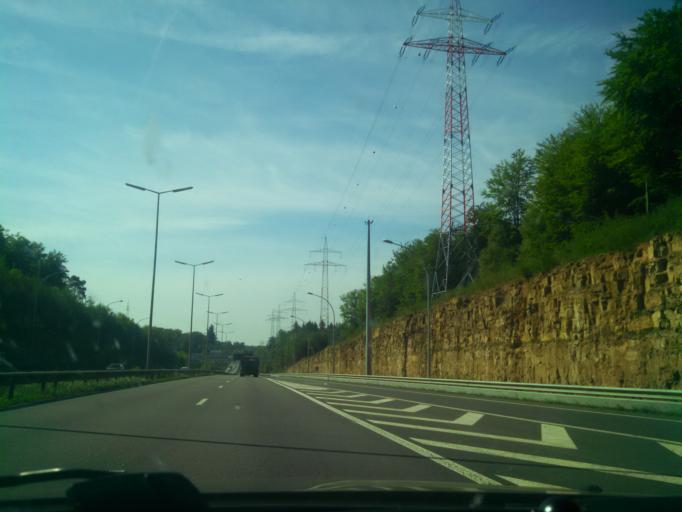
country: LU
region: Luxembourg
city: Kirchberg
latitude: 49.6497
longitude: 6.1861
